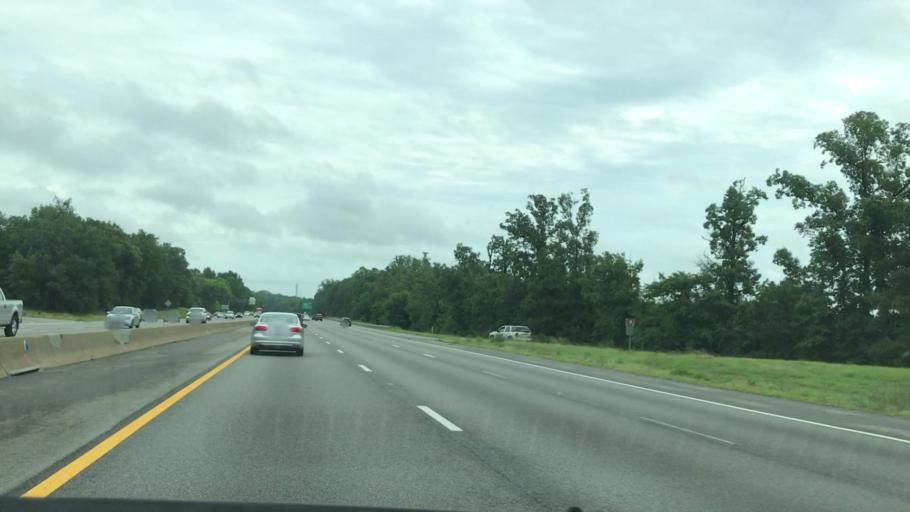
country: US
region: Virginia
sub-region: Chesterfield County
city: Chester
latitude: 37.3564
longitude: -77.4043
